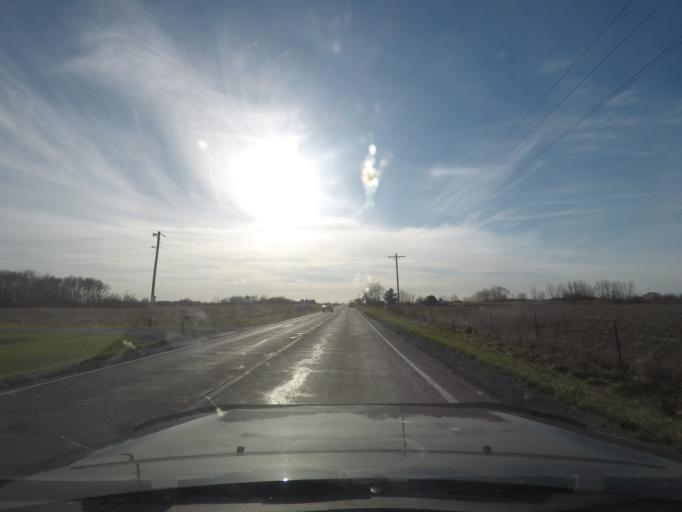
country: US
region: Indiana
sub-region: Marshall County
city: Plymouth
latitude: 41.4490
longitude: -86.3400
